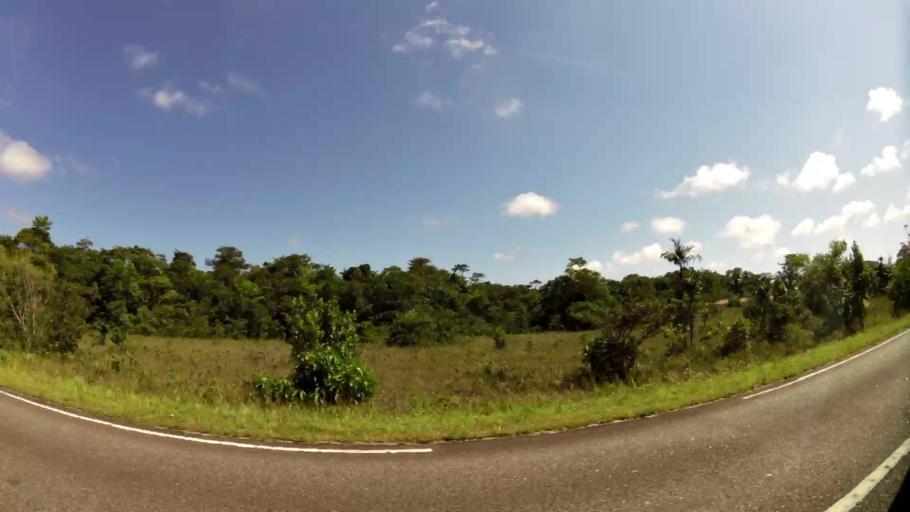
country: GF
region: Guyane
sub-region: Guyane
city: Matoury
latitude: 4.8296
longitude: -52.3533
